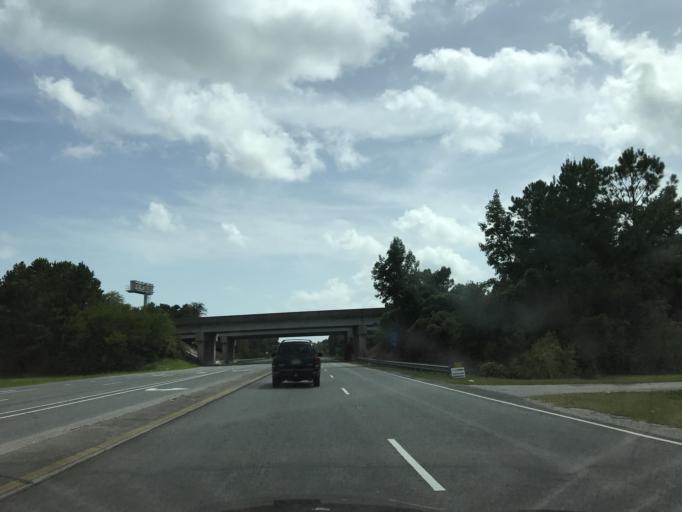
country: US
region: North Carolina
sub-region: New Hanover County
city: Wrightsboro
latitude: 34.3183
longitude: -77.9226
